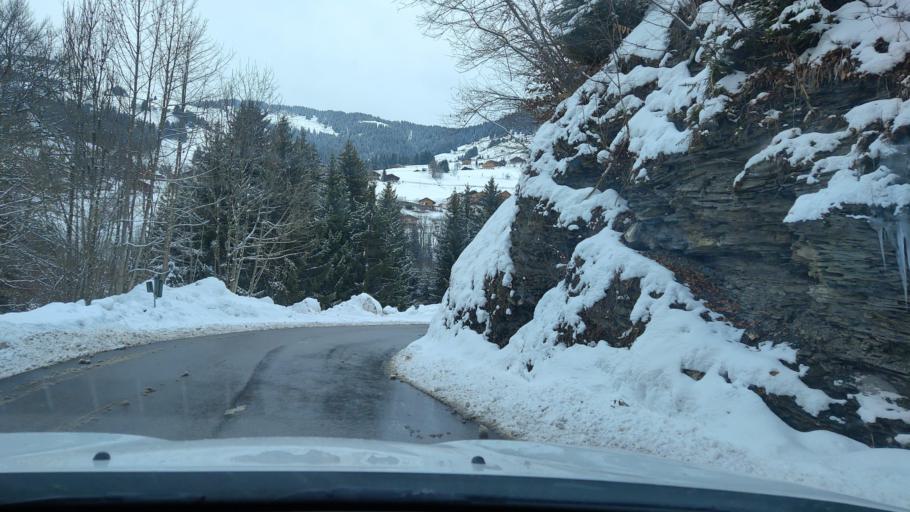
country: FR
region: Rhone-Alpes
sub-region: Departement de la Savoie
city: Beaufort
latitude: 45.7453
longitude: 6.5882
